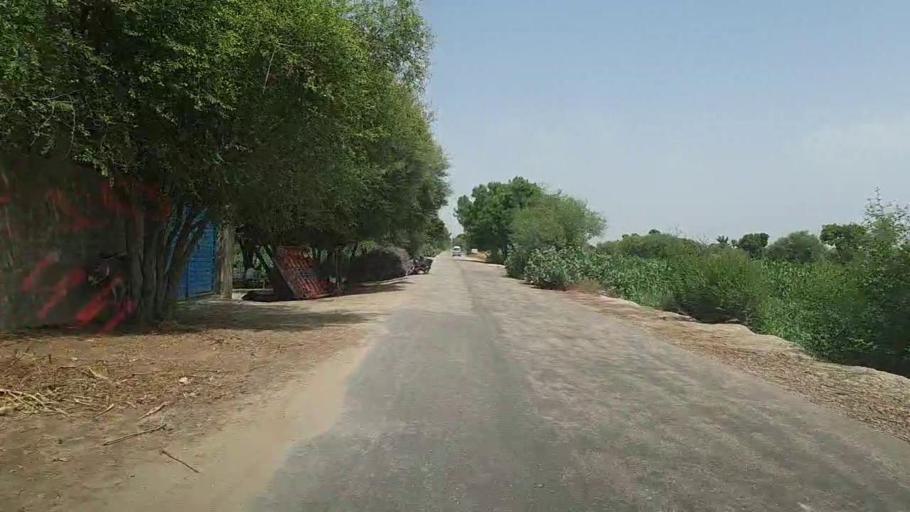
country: PK
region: Sindh
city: Karaundi
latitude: 26.8430
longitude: 68.3471
